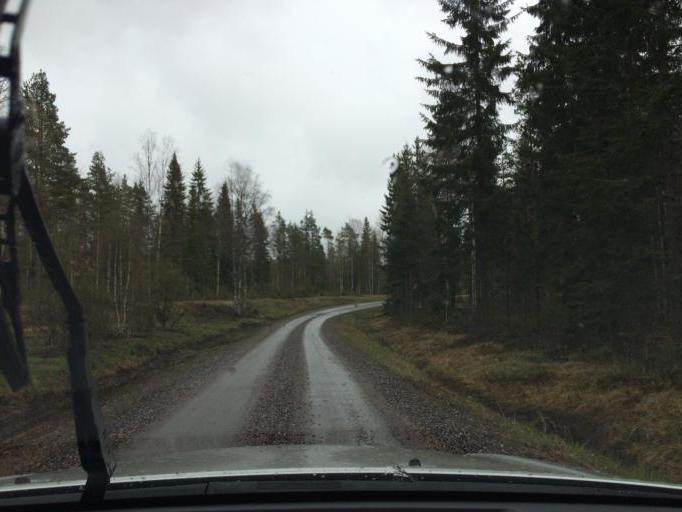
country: SE
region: OErebro
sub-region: Hallefors Kommun
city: Haellefors
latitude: 60.0379
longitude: 14.5290
